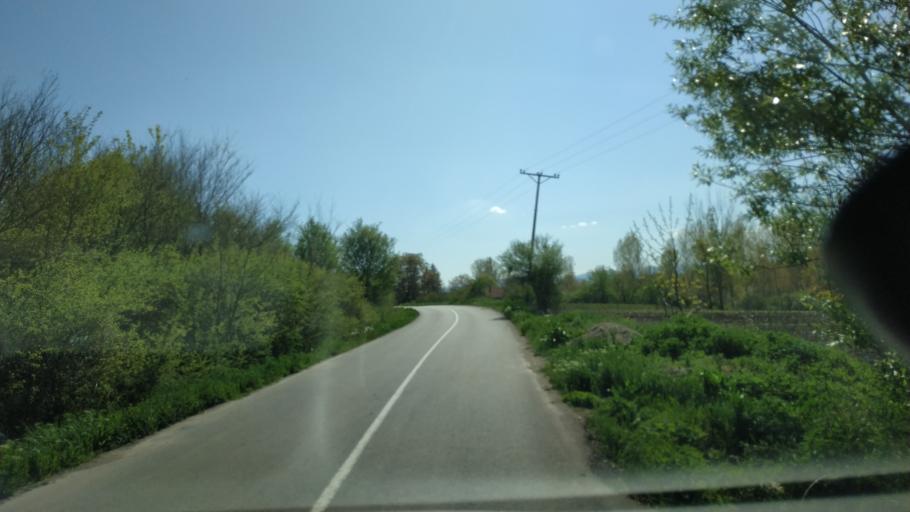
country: RS
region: Central Serbia
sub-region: Nisavski Okrug
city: Nis
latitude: 43.4588
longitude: 21.8553
